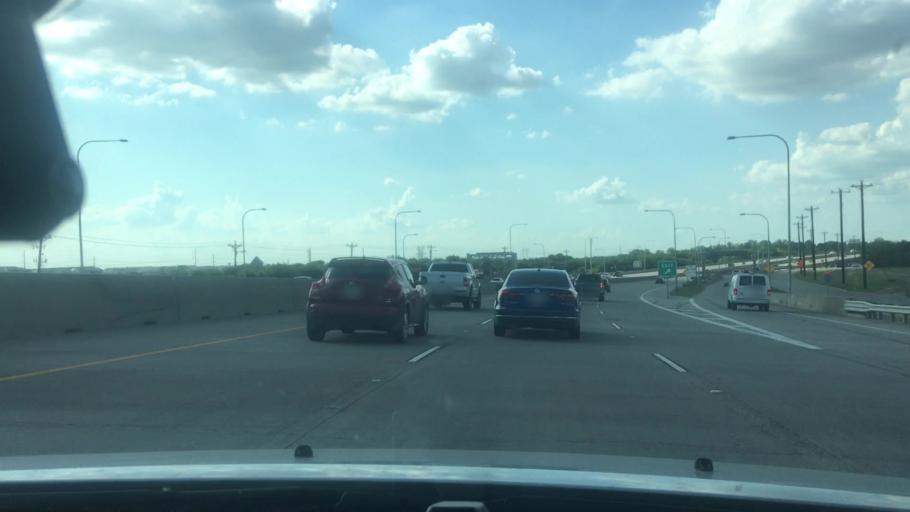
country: US
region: Texas
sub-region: Collin County
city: Frisco
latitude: 33.1391
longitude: -96.8372
